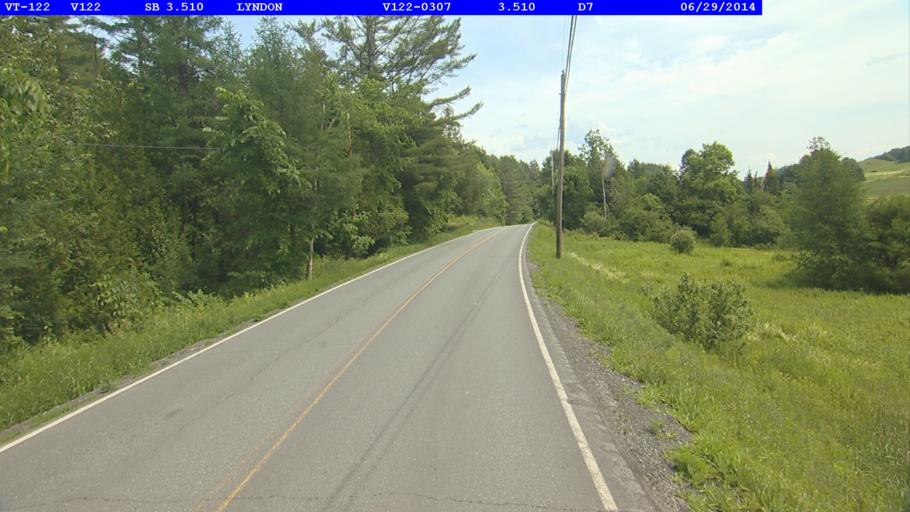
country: US
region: Vermont
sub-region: Caledonia County
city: Lyndonville
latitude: 44.5730
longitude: -72.0492
